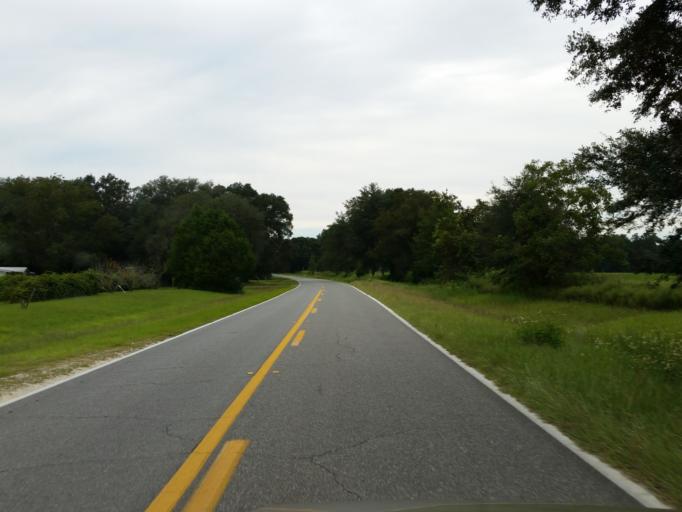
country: US
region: Florida
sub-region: Alachua County
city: High Springs
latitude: 29.9514
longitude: -82.5373
